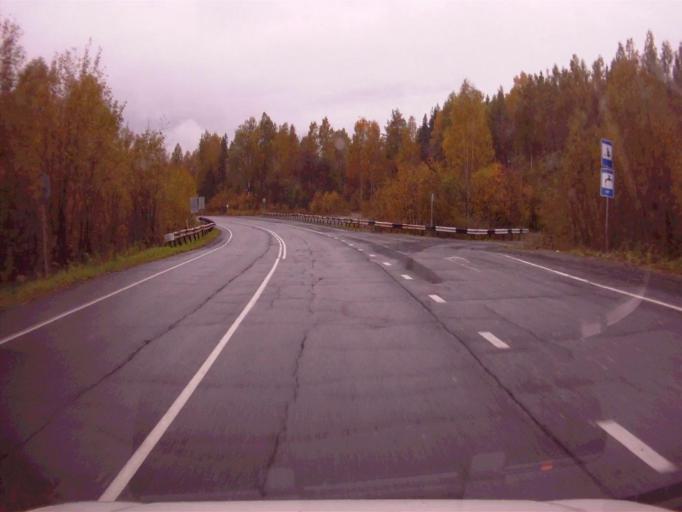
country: RU
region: Chelyabinsk
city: Nizhniy Ufaley
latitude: 56.0674
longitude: 60.0182
